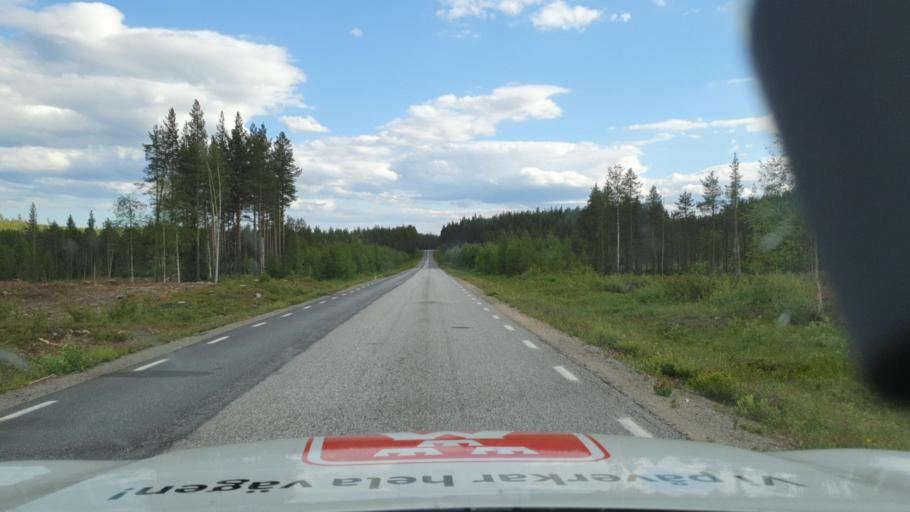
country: SE
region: Vaesterbotten
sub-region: Skelleftea Kommun
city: Langsele
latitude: 64.6010
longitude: 19.9316
